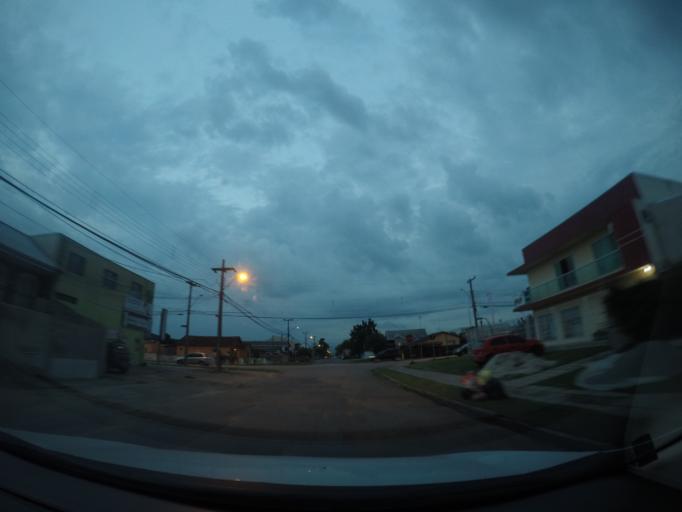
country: BR
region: Parana
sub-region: Sao Jose Dos Pinhais
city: Sao Jose dos Pinhais
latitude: -25.4991
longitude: -49.2332
